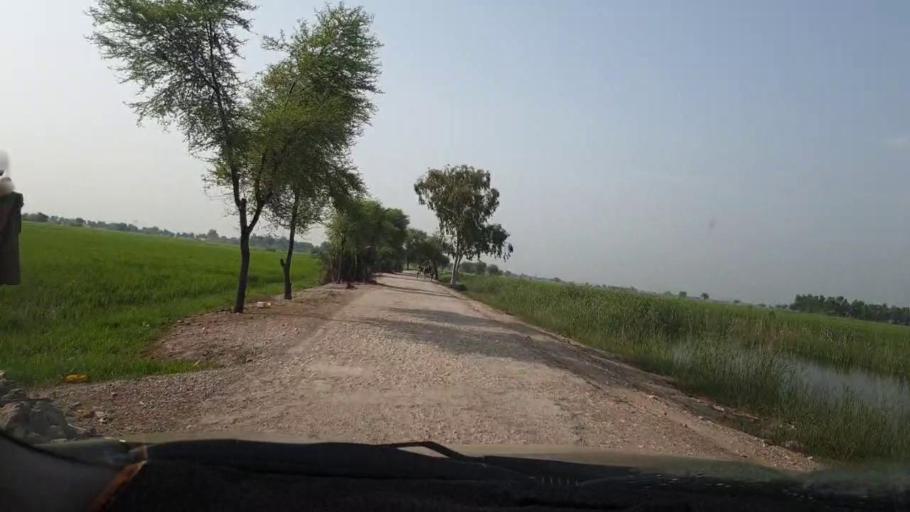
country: PK
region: Sindh
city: Goth Garelo
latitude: 27.4696
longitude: 68.0887
